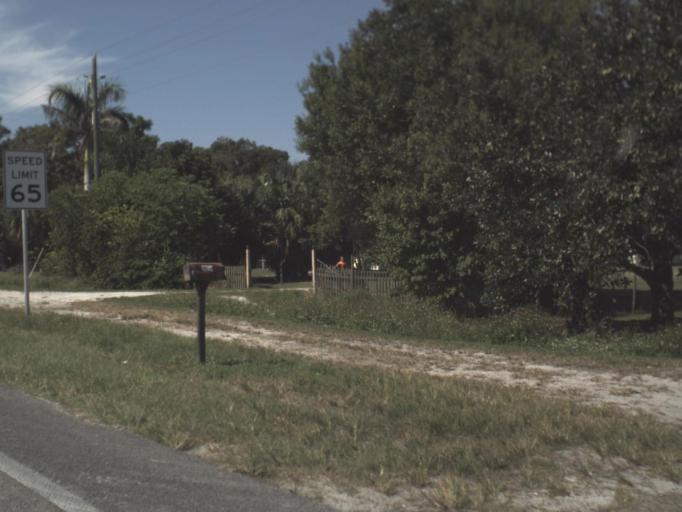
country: US
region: Florida
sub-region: Hendry County
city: Harlem
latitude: 26.7544
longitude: -80.9802
